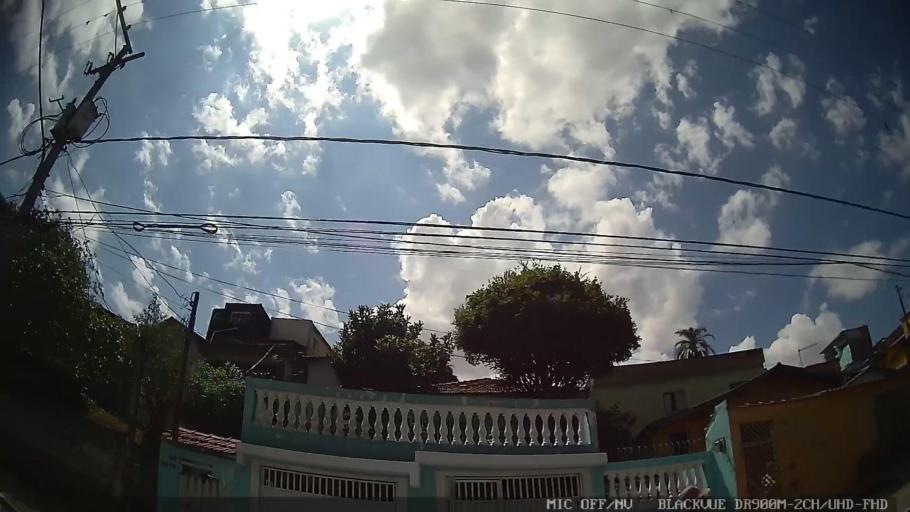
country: BR
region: Sao Paulo
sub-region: Ferraz De Vasconcelos
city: Ferraz de Vasconcelos
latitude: -23.5423
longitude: -46.4617
